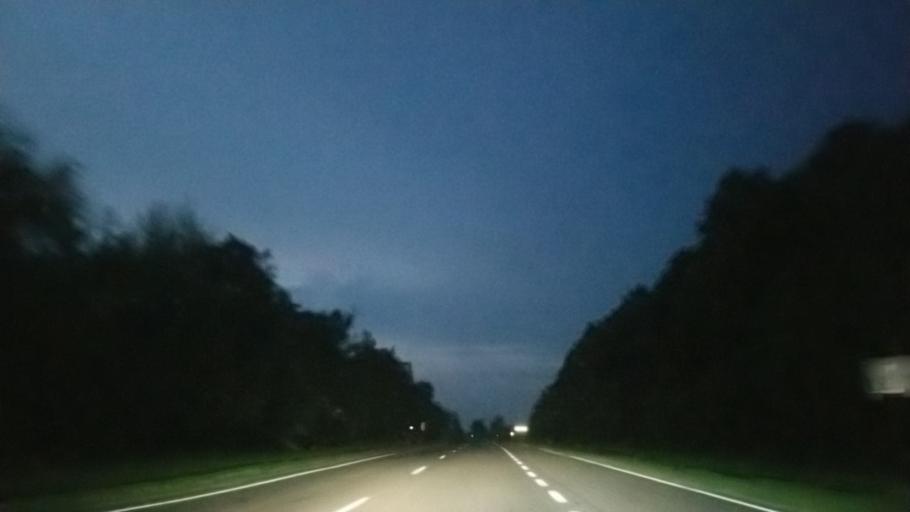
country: PL
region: Lublin Voivodeship
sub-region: Powiat bialski
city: Koden
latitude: 51.9185
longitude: 23.6594
